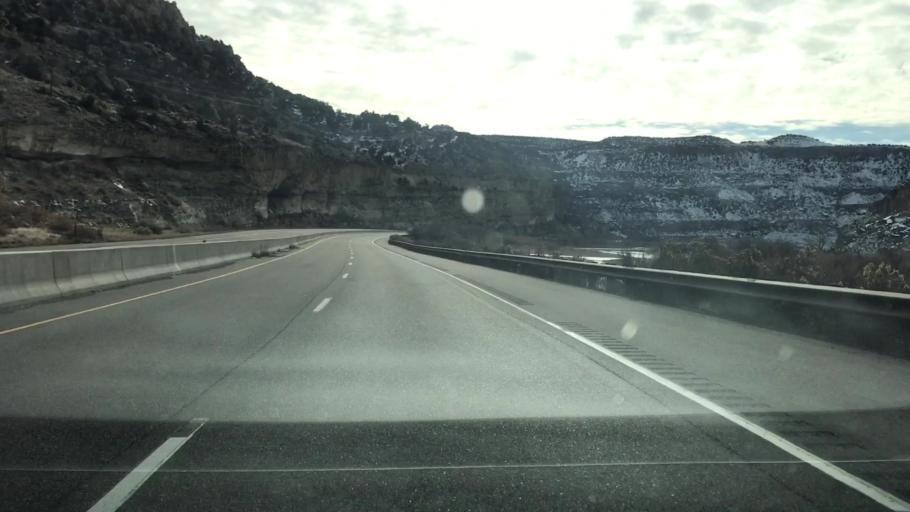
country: US
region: Colorado
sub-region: Mesa County
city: Palisade
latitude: 39.2527
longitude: -108.2589
